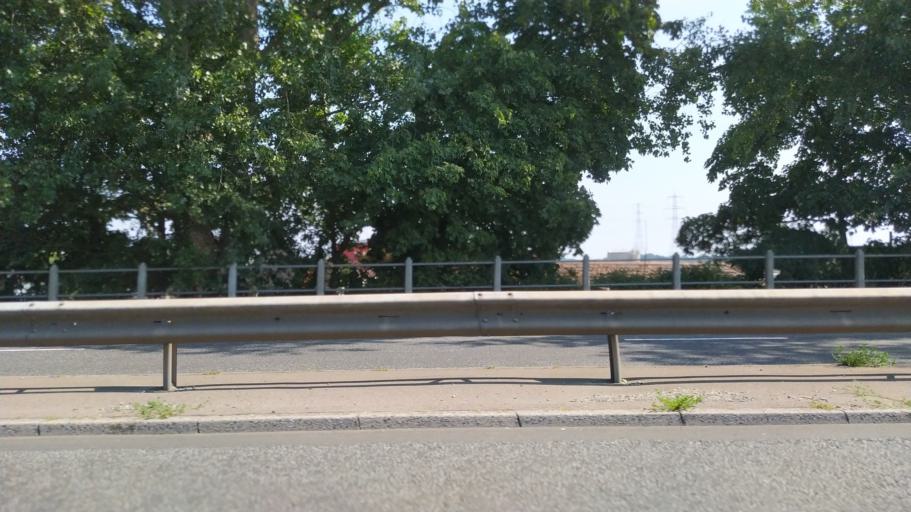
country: GB
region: England
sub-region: Hampshire
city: Totton
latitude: 50.9169
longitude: -1.4817
